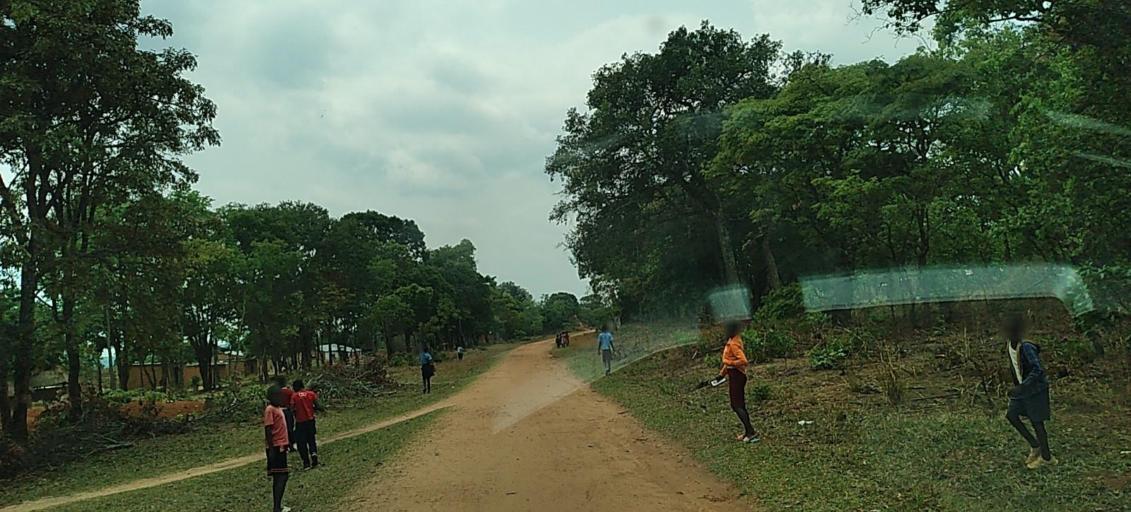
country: ZM
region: North-Western
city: Mwinilunga
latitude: -11.5242
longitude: 24.7872
